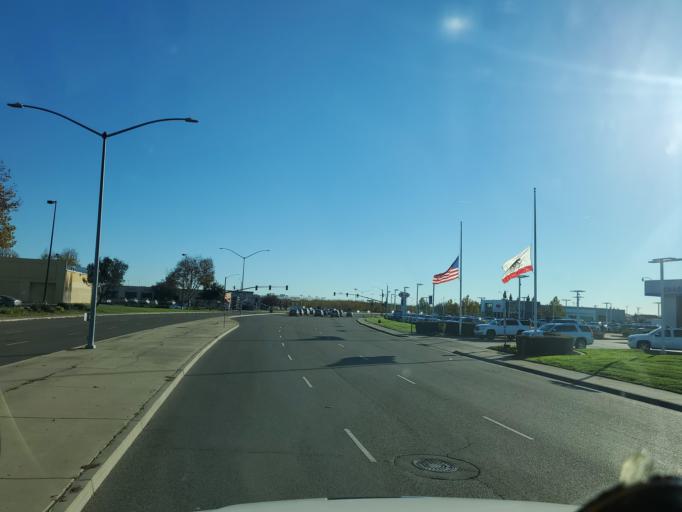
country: US
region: California
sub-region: San Joaquin County
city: Morada
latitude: 38.0189
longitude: -121.2707
